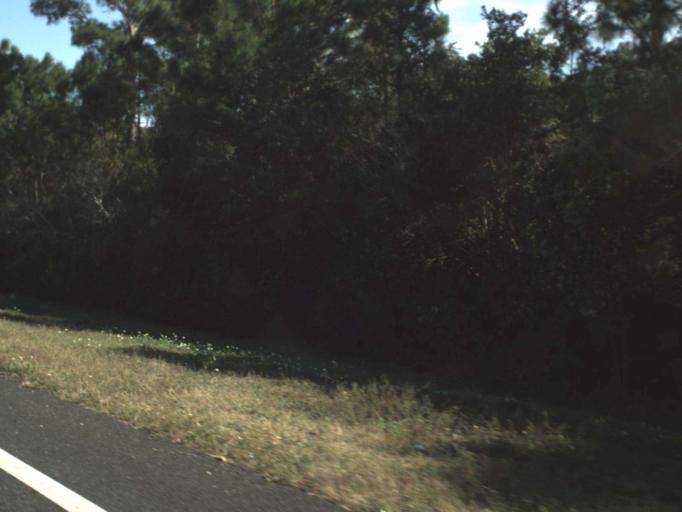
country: US
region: Florida
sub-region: Walton County
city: Miramar Beach
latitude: 30.3847
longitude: -86.3692
